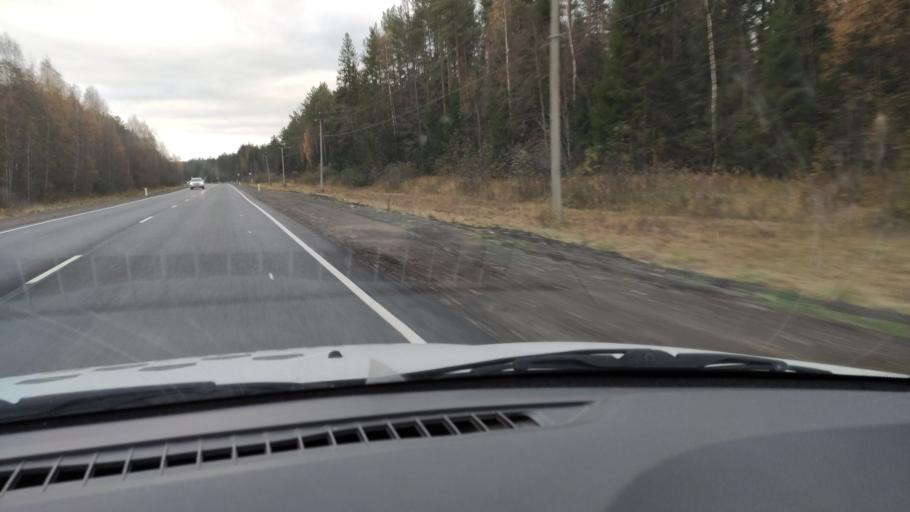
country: RU
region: Kirov
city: Belaya Kholunitsa
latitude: 58.8439
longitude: 50.7682
